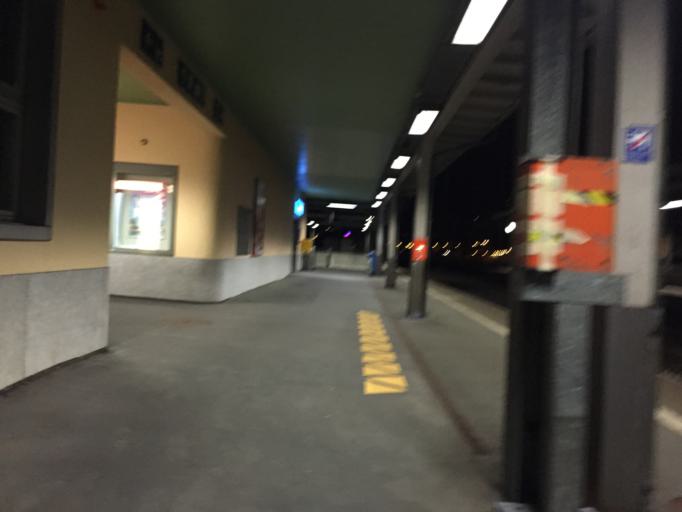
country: CH
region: Uri
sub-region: Uri
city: Flueelen
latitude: 46.9017
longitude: 8.6244
